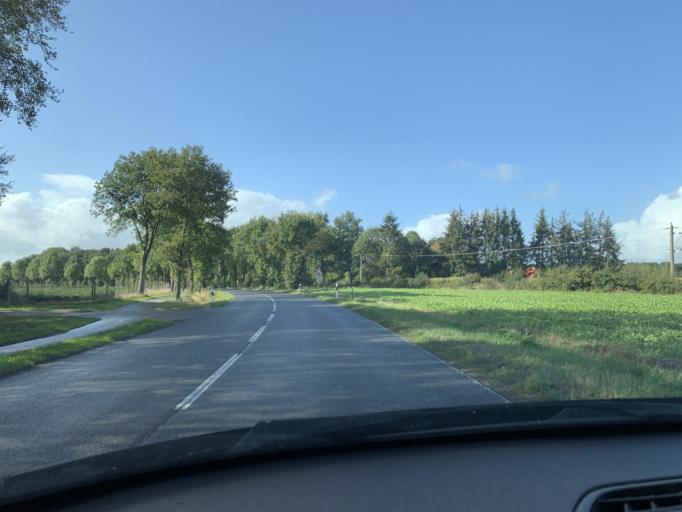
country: DE
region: Lower Saxony
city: Westerstede
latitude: 53.1965
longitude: 7.9136
